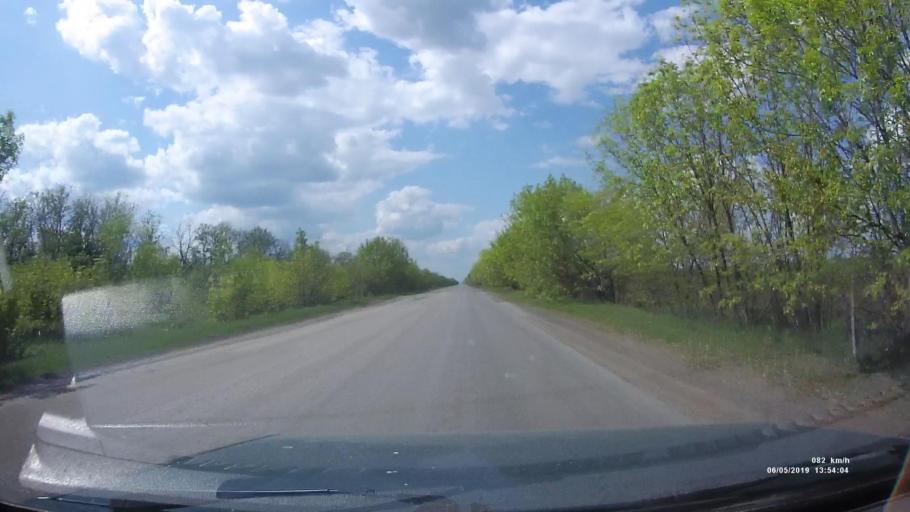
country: RU
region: Rostov
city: Melikhovskaya
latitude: 47.6723
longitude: 40.4527
